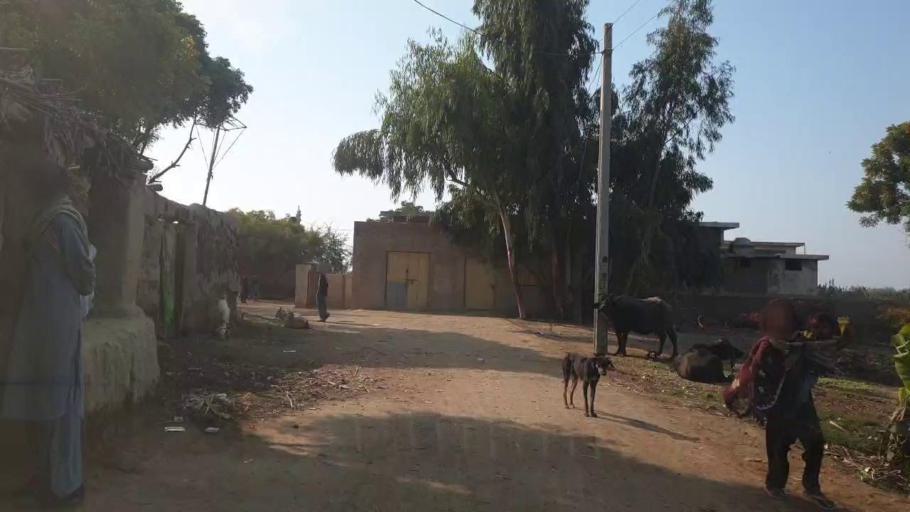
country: PK
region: Sindh
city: Tando Allahyar
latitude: 25.5602
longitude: 68.7547
